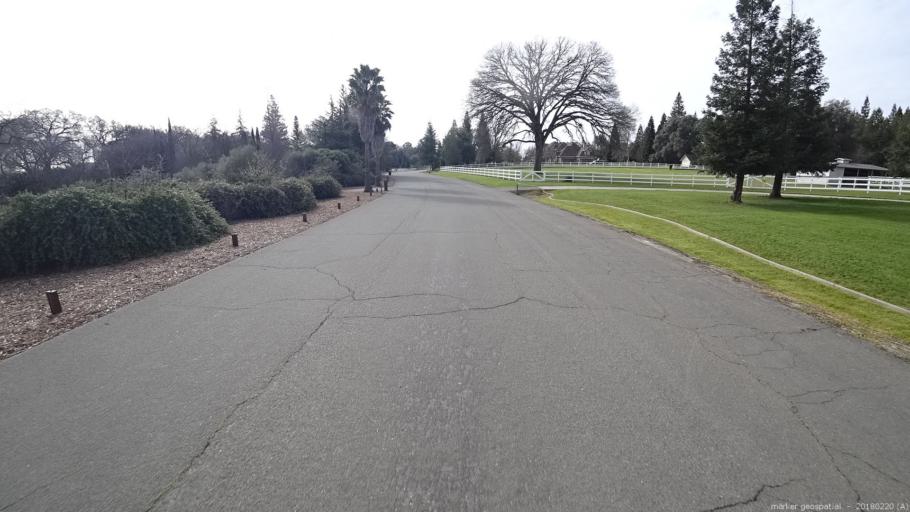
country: US
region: California
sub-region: Sacramento County
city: Orangevale
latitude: 38.7037
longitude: -121.2305
